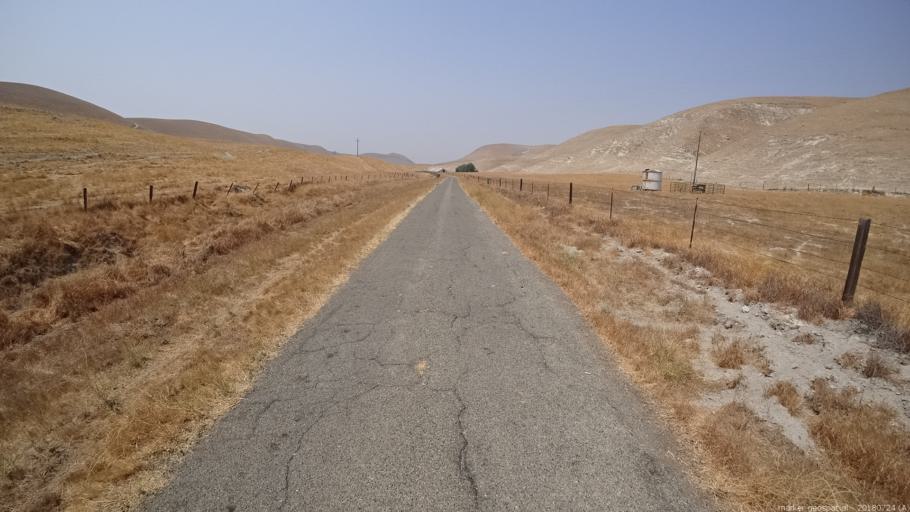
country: US
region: California
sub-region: Monterey County
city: King City
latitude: 36.1908
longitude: -120.9759
